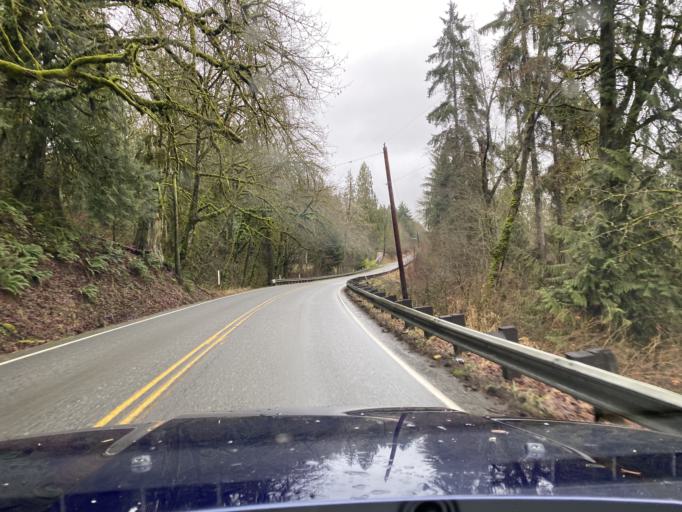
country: US
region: Washington
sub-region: King County
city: Duvall
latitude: 47.7552
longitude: -122.0050
